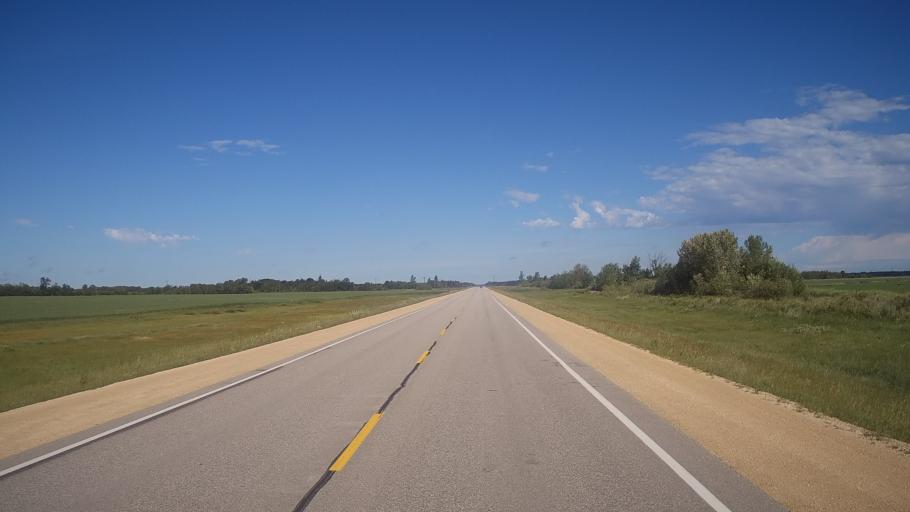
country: CA
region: Manitoba
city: Stonewall
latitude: 50.1901
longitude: -97.6361
